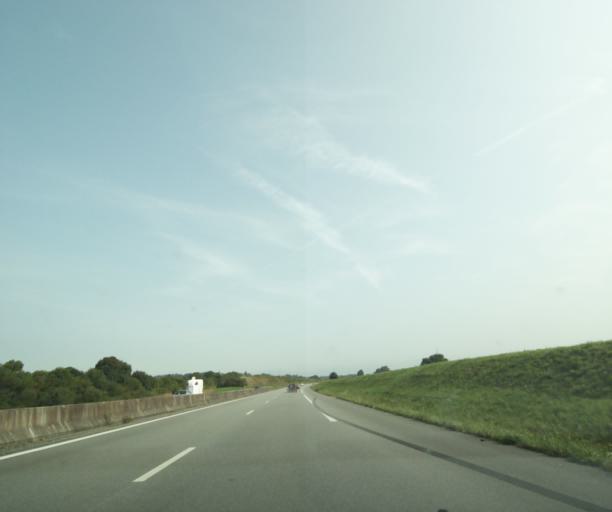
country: FR
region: Lower Normandy
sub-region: Departement de l'Orne
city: Radon
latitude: 48.5075
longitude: 0.1314
